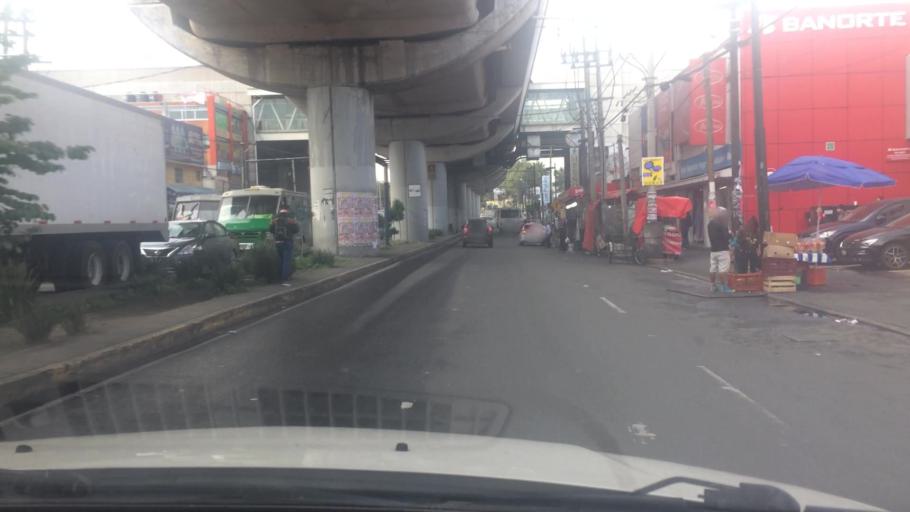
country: MX
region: Mexico City
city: Iztapalapa
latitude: 19.3378
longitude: -99.1090
